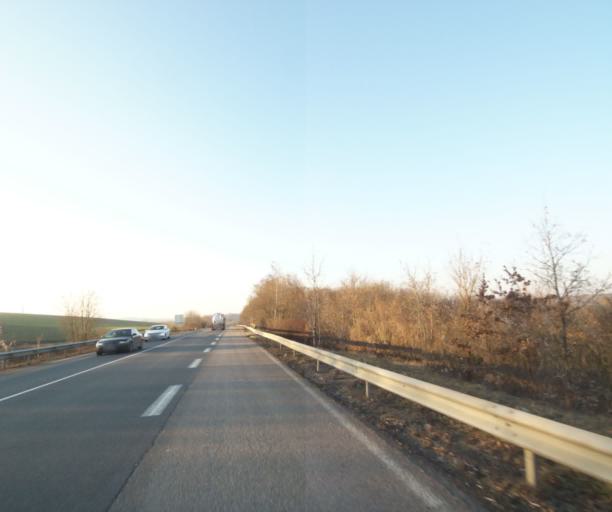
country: FR
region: Champagne-Ardenne
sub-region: Departement de la Haute-Marne
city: Bienville
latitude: 48.5427
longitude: 5.0828
